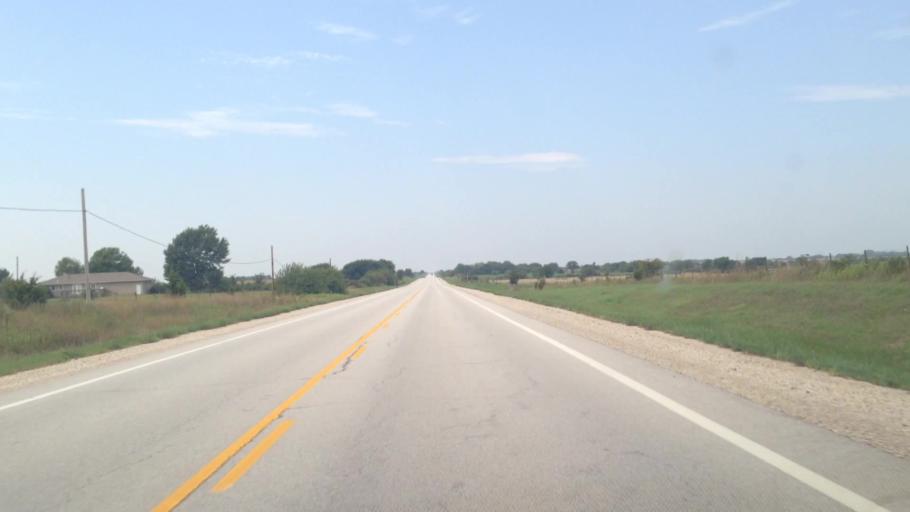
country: US
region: Kansas
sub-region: Anderson County
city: Garnett
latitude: 38.0816
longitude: -95.1849
